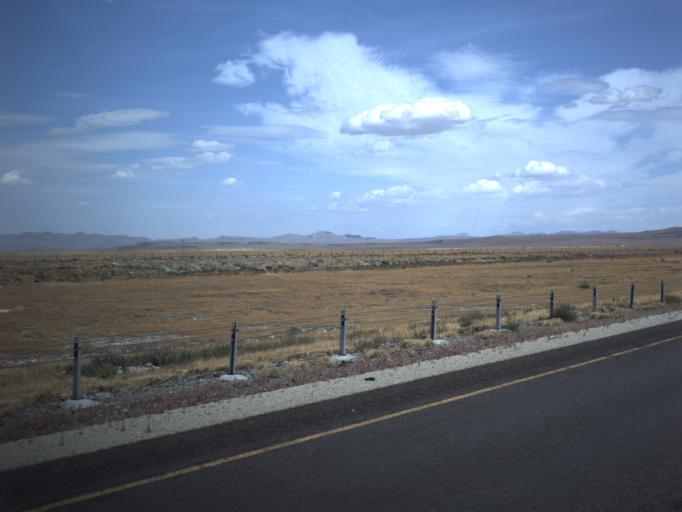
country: US
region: Utah
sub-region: Tooele County
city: Wendover
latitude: 40.7264
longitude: -113.2511
